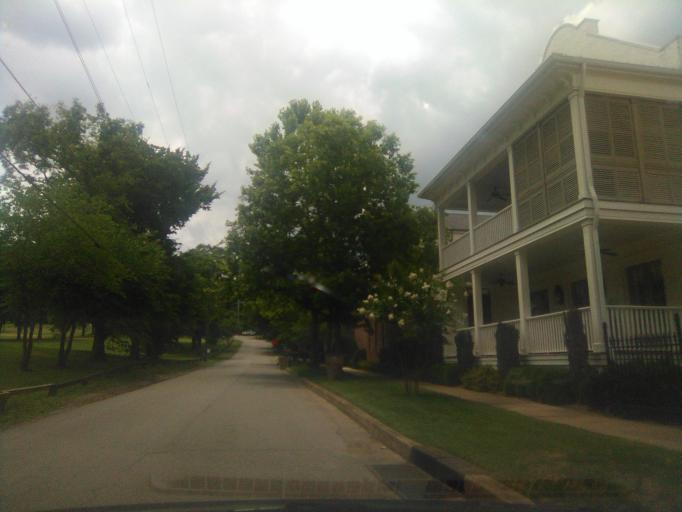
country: US
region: Tennessee
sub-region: Davidson County
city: Belle Meade
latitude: 36.0859
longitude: -86.8703
